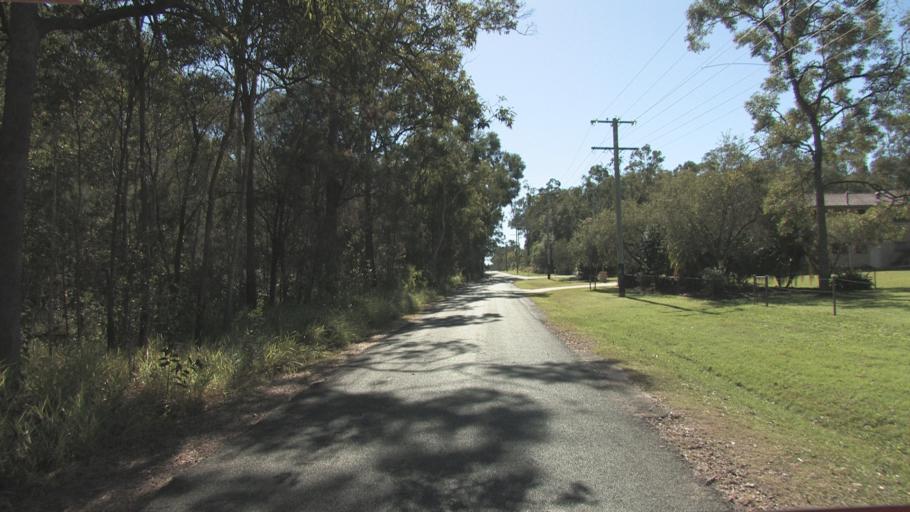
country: AU
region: Queensland
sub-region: Logan
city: Park Ridge South
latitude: -27.6943
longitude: 153.0048
